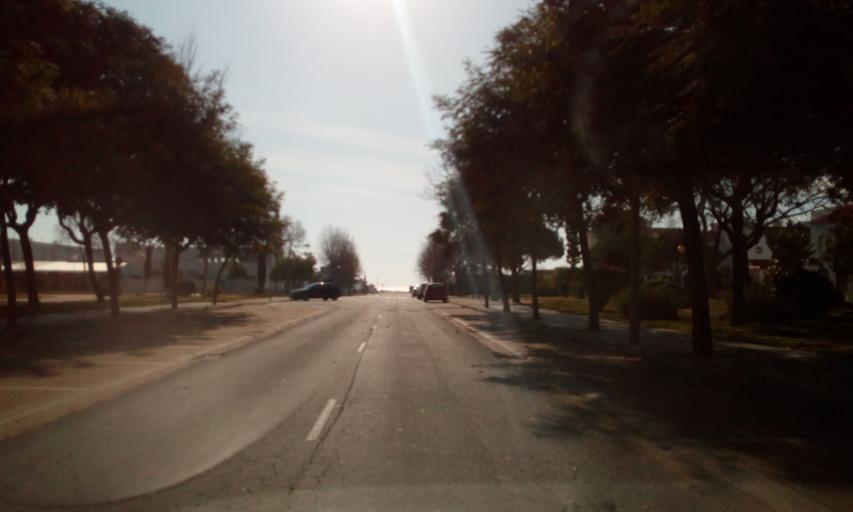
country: ES
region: Andalusia
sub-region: Provincia de Huelva
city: Lepe
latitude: 37.2086
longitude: -7.2032
